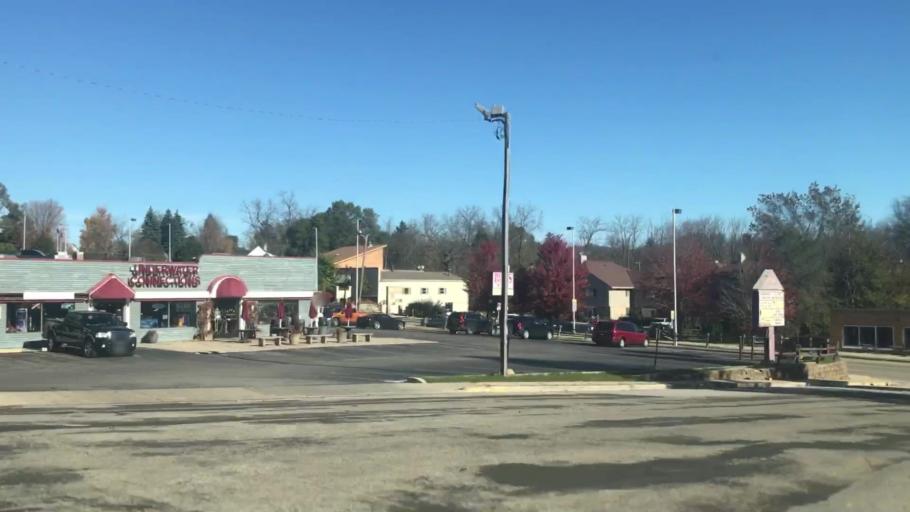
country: US
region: Wisconsin
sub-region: Waukesha County
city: Menomonee Falls
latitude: 43.1750
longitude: -88.1142
